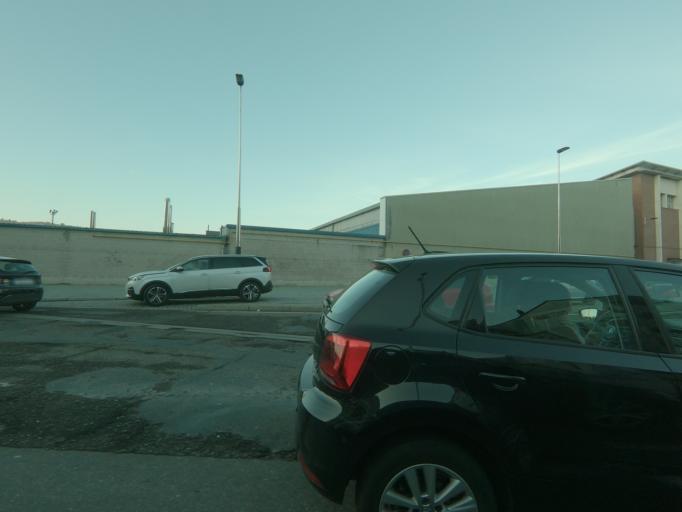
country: ES
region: Galicia
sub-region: Provincia de Ourense
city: Ourense
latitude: 42.3431
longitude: -7.8713
